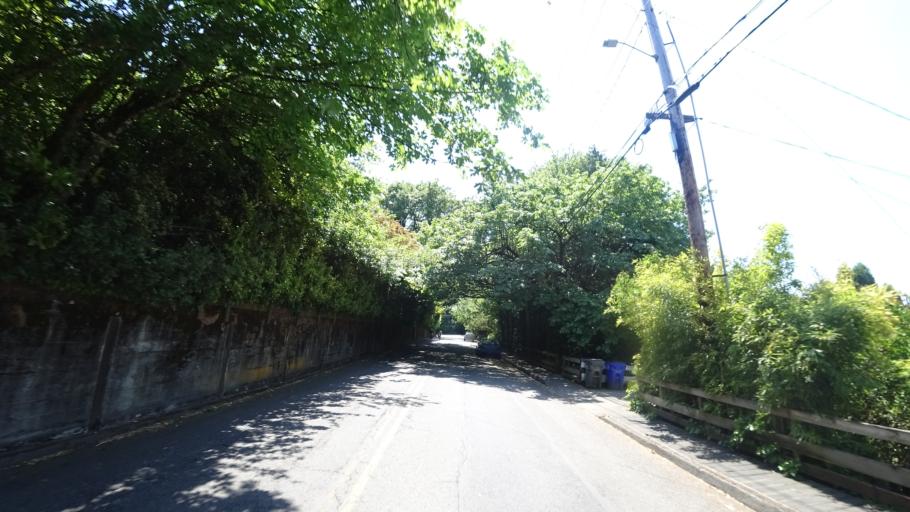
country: US
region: Oregon
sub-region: Multnomah County
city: Portland
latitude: 45.5033
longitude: -122.7052
